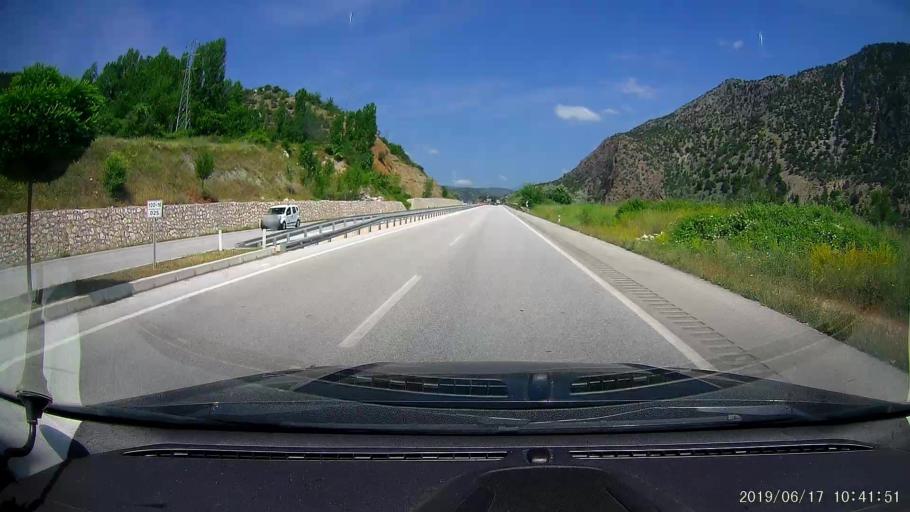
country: TR
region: Corum
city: Kargi
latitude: 41.0437
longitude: 34.5668
